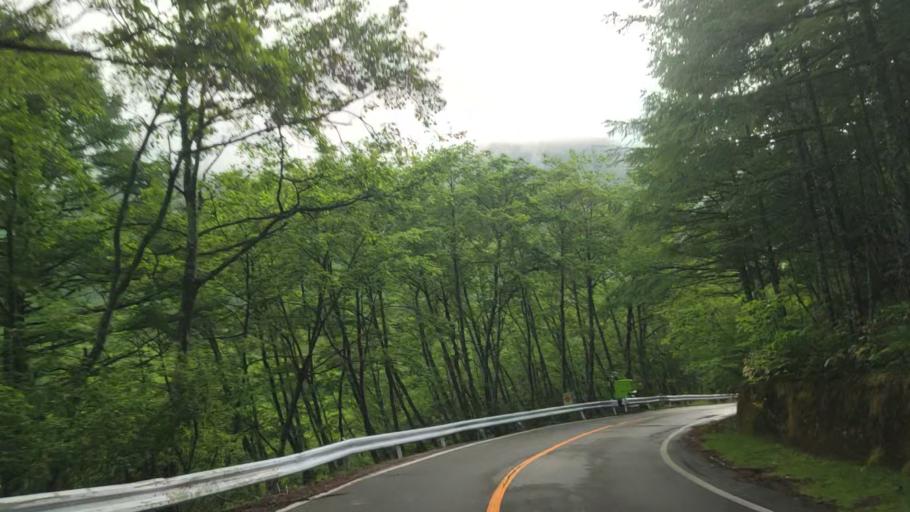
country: JP
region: Nagano
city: Chino
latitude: 36.0942
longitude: 138.2739
